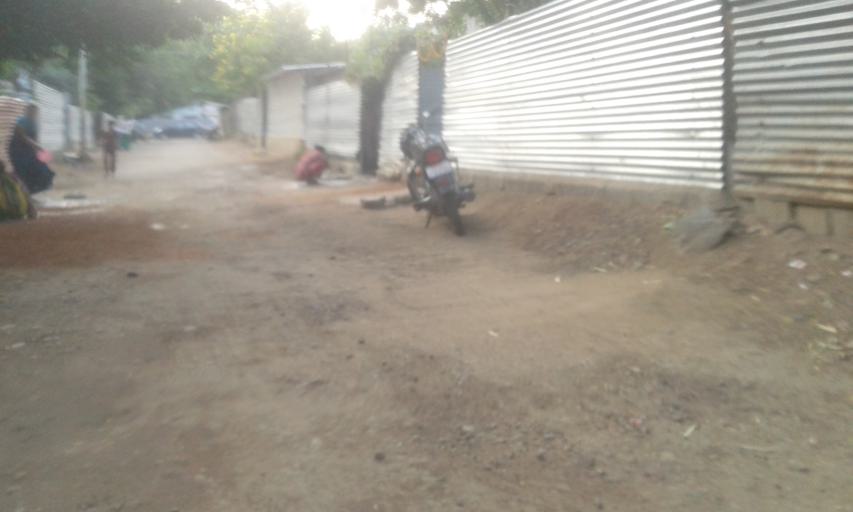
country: IN
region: Karnataka
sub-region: Raichur
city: Lingsugur
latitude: 16.1933
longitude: 76.6623
